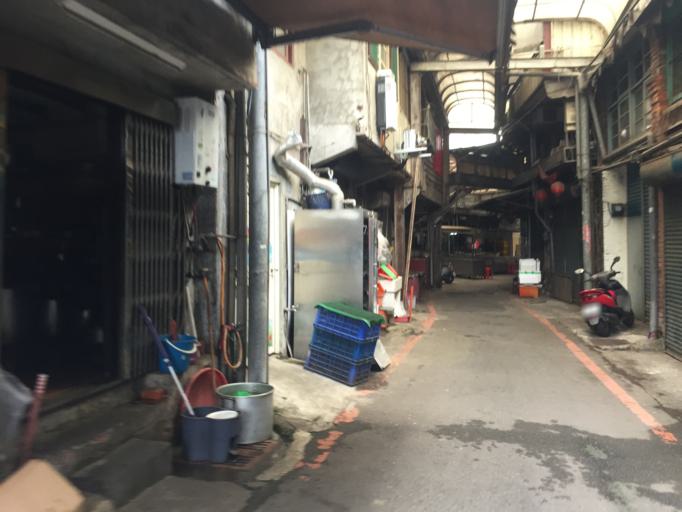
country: TW
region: Taiwan
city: Daxi
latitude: 24.7905
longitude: 121.1757
